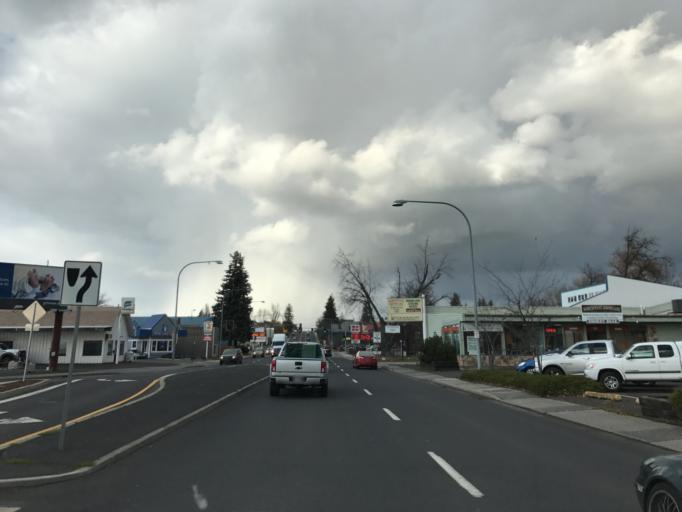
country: US
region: Idaho
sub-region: Latah County
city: Moscow
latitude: 46.7360
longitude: -117.0014
